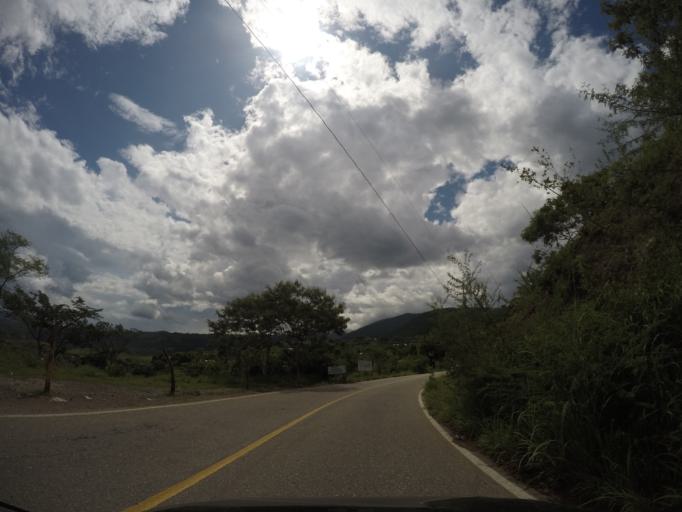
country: MX
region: Oaxaca
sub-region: San Jeronimo Coatlan
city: San Cristobal Honduras
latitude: 16.4332
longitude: -97.0612
